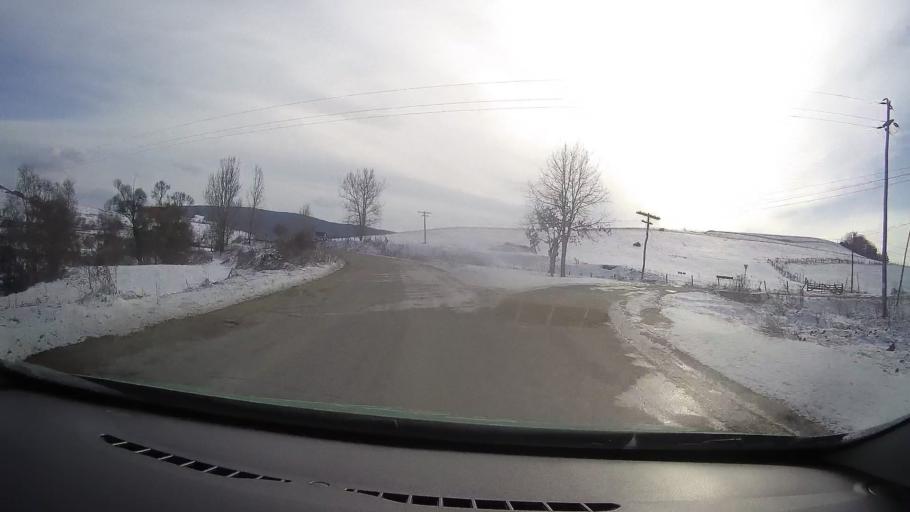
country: RO
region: Sibiu
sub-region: Oras Agnita
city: Ruja
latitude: 46.0016
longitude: 24.6726
